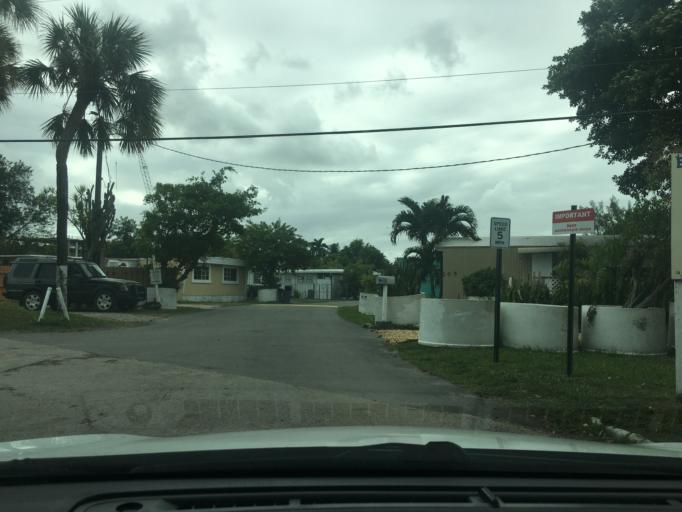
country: US
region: Florida
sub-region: Miami-Dade County
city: Biscayne Park
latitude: 25.8812
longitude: -80.1671
